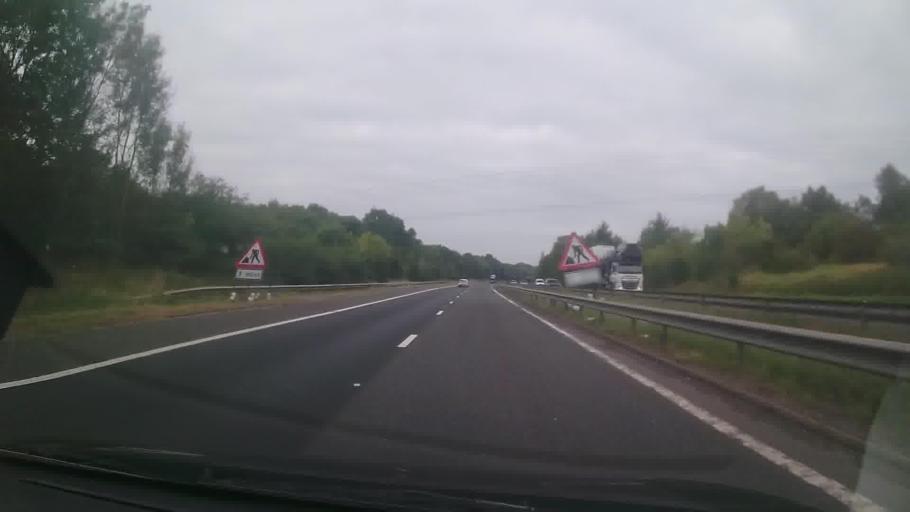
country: GB
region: Scotland
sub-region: South Lanarkshire
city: Larkhall
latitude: 55.7433
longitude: -3.9571
